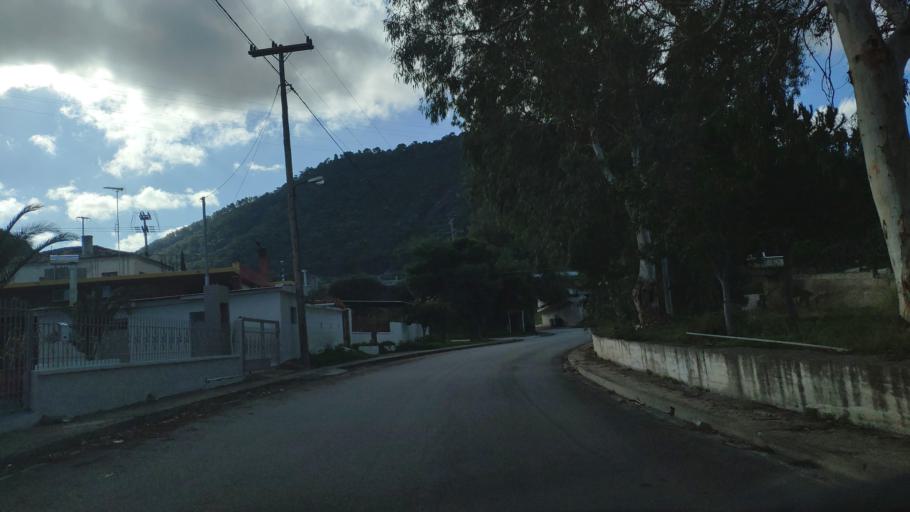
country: GR
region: West Greece
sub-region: Nomos Achaias
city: Aiyira
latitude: 38.1346
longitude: 22.4283
